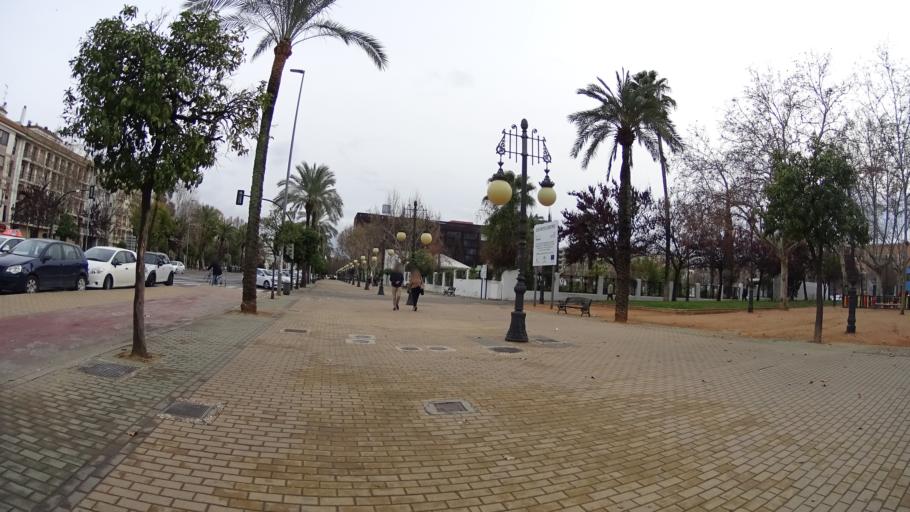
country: ES
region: Andalusia
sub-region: Province of Cordoba
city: Cordoba
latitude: 37.8829
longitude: -4.7851
